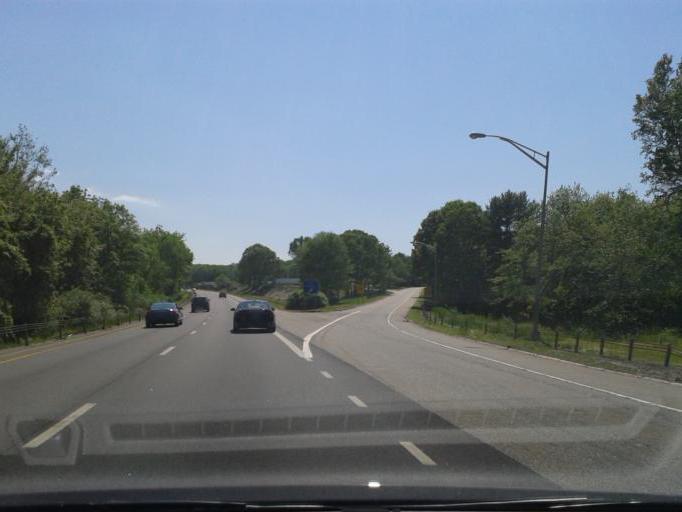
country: US
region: Connecticut
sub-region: New London County
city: Pawcatuck
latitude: 41.4184
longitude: -71.8483
